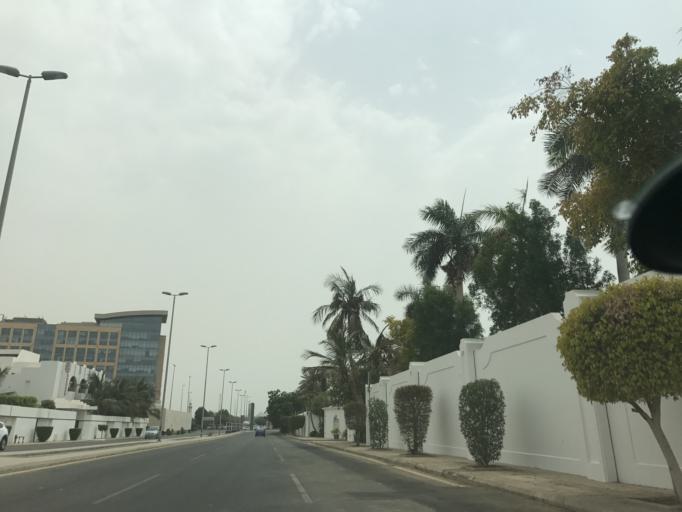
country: SA
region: Makkah
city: Jeddah
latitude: 21.5520
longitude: 39.1522
